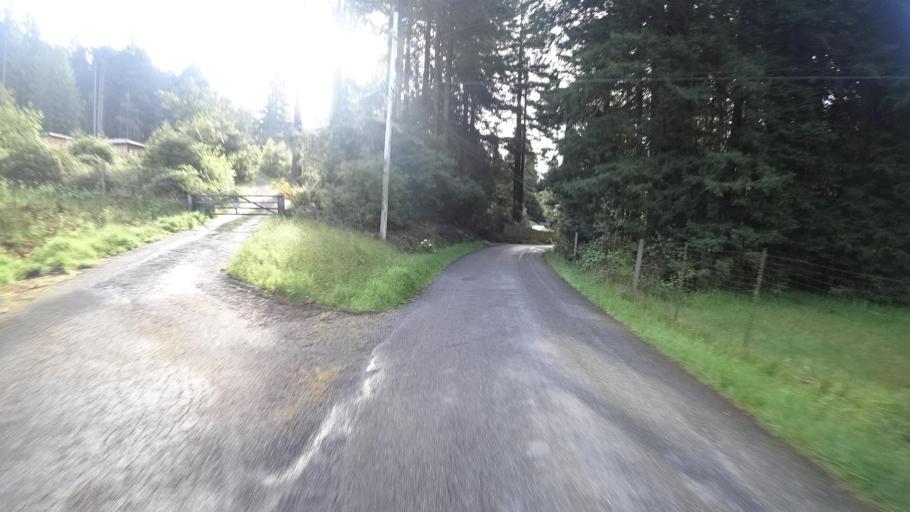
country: US
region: California
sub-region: Humboldt County
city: Blue Lake
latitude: 40.8836
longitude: -124.0244
